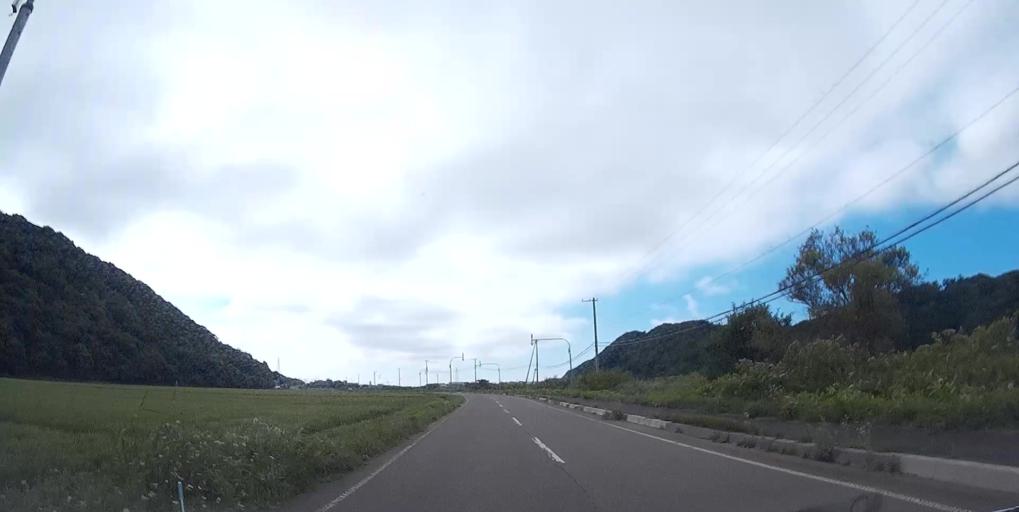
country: JP
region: Hokkaido
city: Kamiiso
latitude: 41.9722
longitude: 140.1548
